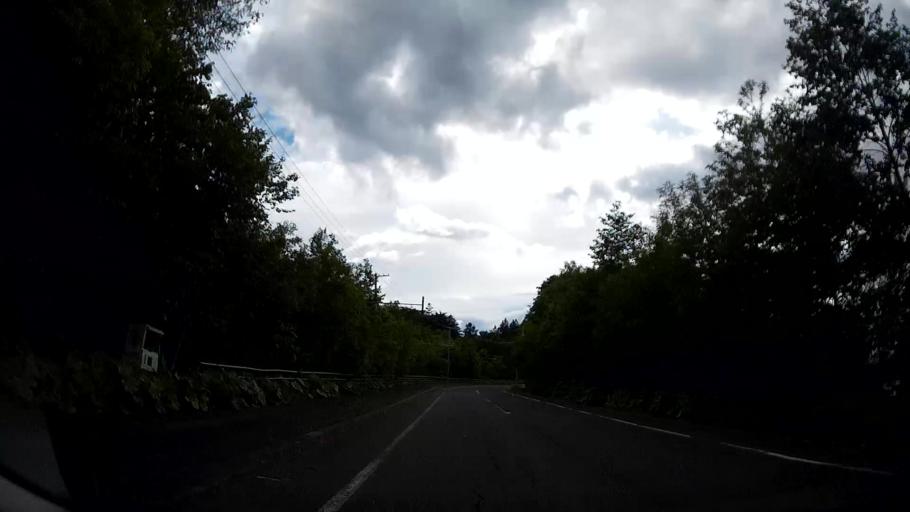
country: JP
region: Hokkaido
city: Kitahiroshima
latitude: 42.8439
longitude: 141.4522
